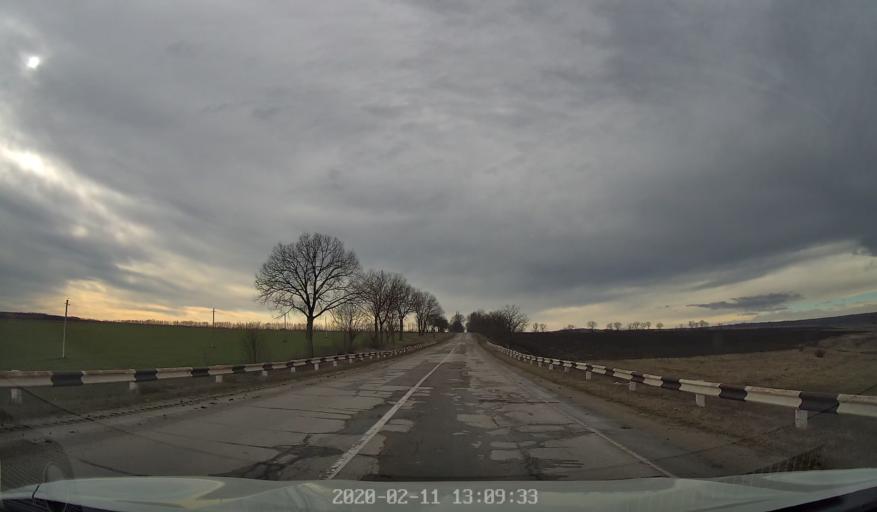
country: RO
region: Botosani
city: Radauti
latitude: 48.2868
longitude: 26.8655
